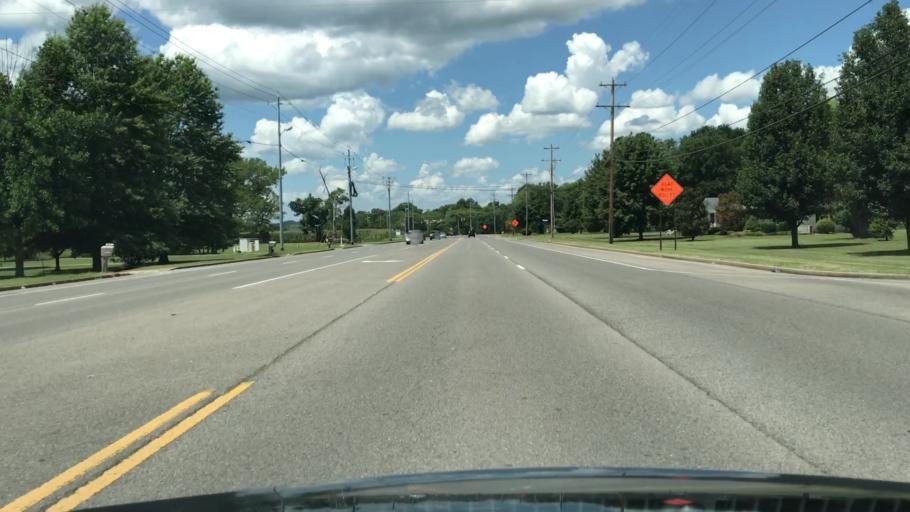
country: US
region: Tennessee
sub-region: Rutherford County
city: Murfreesboro
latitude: 35.8442
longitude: -86.4802
